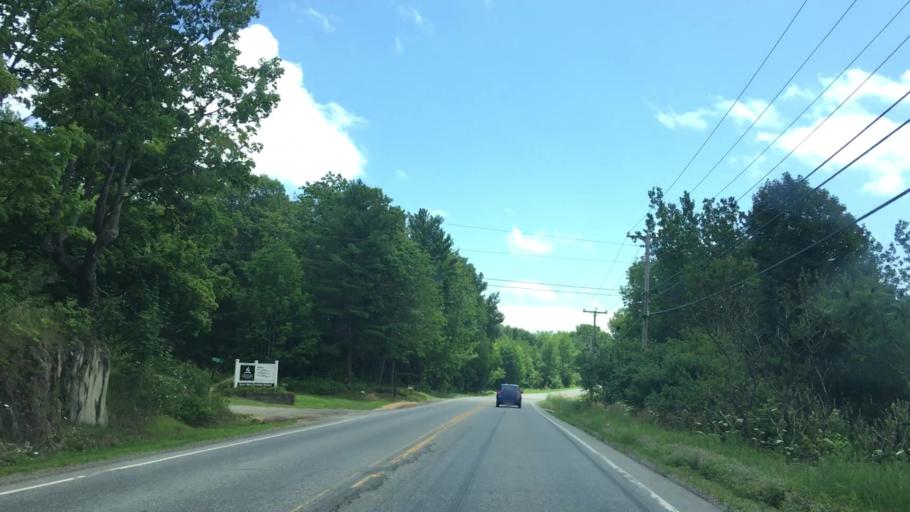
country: US
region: Maine
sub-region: Penobscot County
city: Hermon
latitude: 44.8032
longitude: -68.8968
